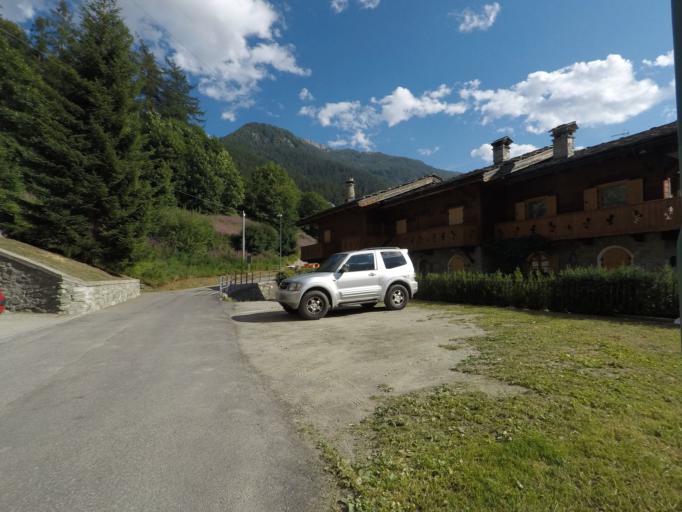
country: IT
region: Aosta Valley
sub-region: Valle d'Aosta
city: Valtournenche
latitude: 45.8755
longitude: 7.6261
